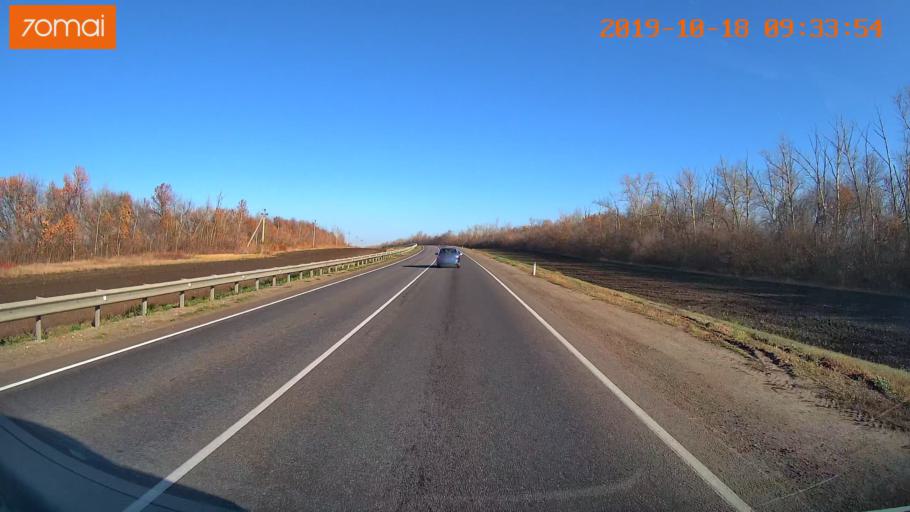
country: RU
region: Tula
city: Yefremov
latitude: 53.1731
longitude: 38.1525
